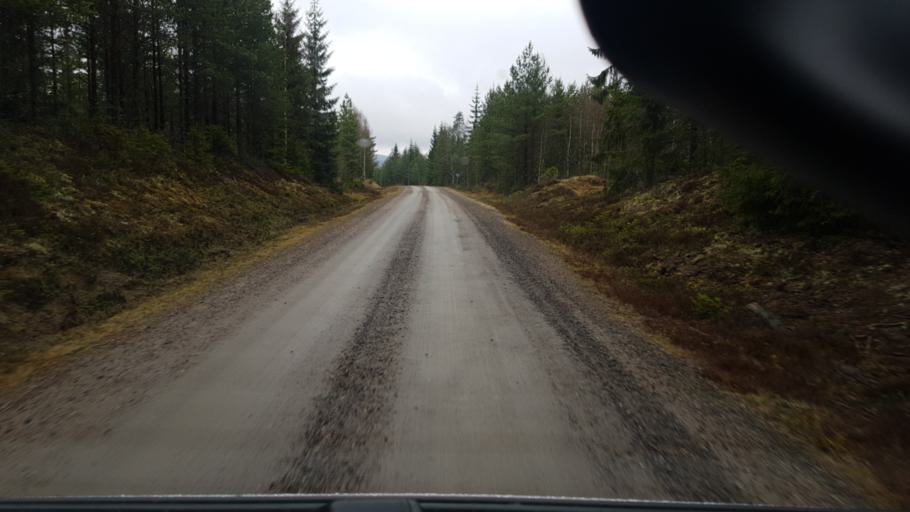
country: SE
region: Vaermland
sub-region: Eda Kommun
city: Charlottenberg
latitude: 59.9841
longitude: 12.4148
